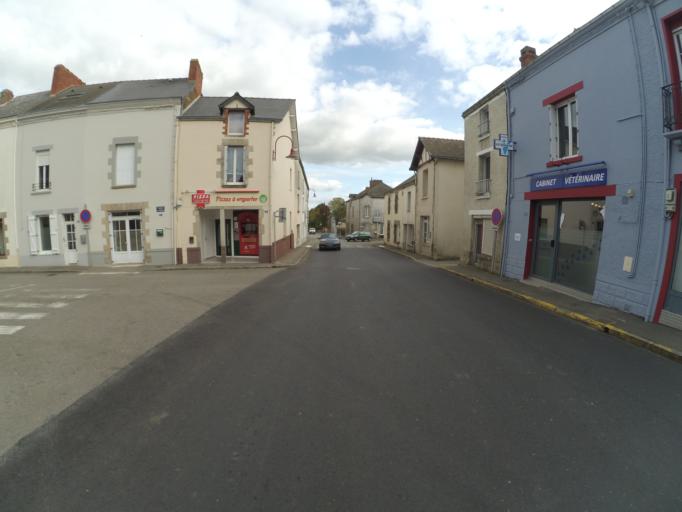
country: FR
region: Pays de la Loire
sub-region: Departement de la Loire-Atlantique
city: Fay-de-Bretagne
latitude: 47.4151
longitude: -1.7914
